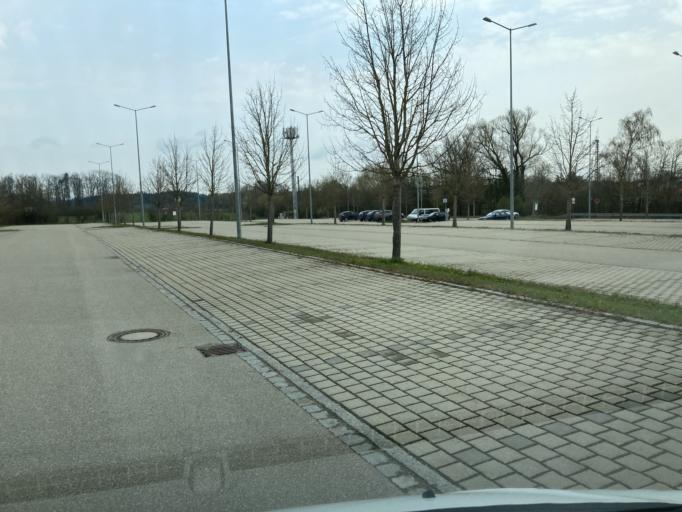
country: DE
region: Bavaria
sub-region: Upper Bavaria
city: Grafing bei Munchen
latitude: 48.0428
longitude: 11.9388
